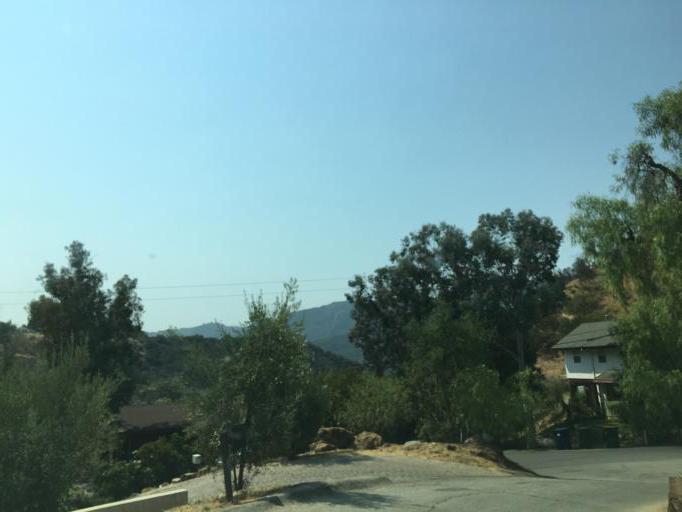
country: US
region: California
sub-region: Los Angeles County
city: Topanga
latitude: 34.1156
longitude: -118.6264
